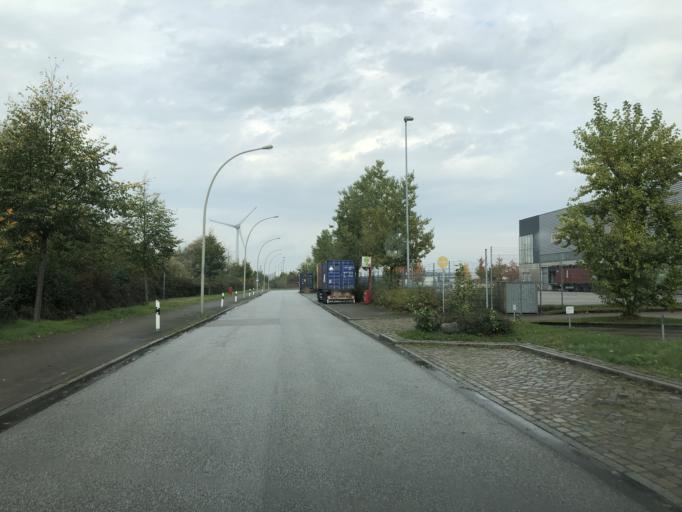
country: DE
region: Hamburg
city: Altona
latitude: 53.4987
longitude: 9.9192
